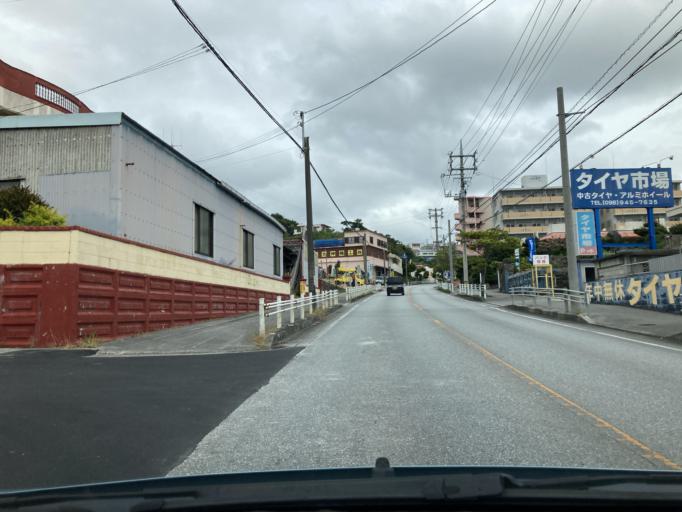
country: JP
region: Okinawa
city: Ginowan
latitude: 26.2325
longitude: 127.7527
